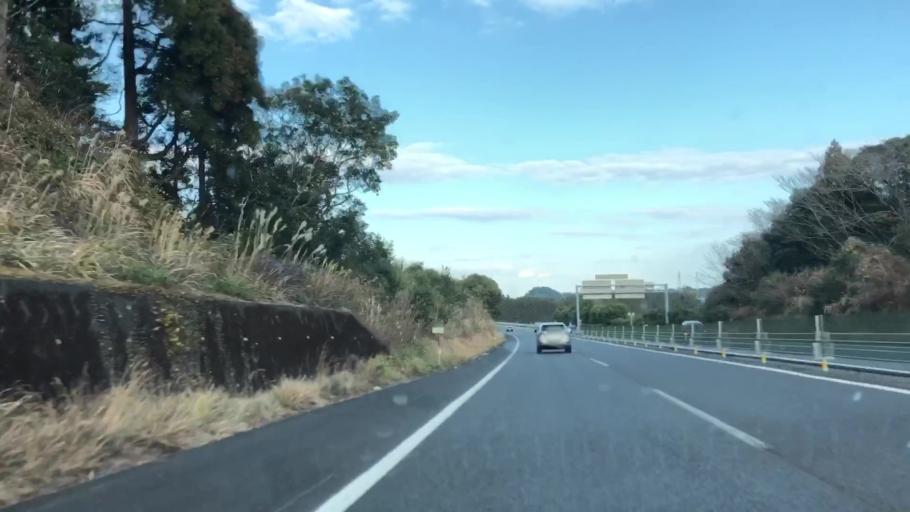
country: JP
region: Miyazaki
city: Miyazaki-shi
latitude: 31.8537
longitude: 131.3708
